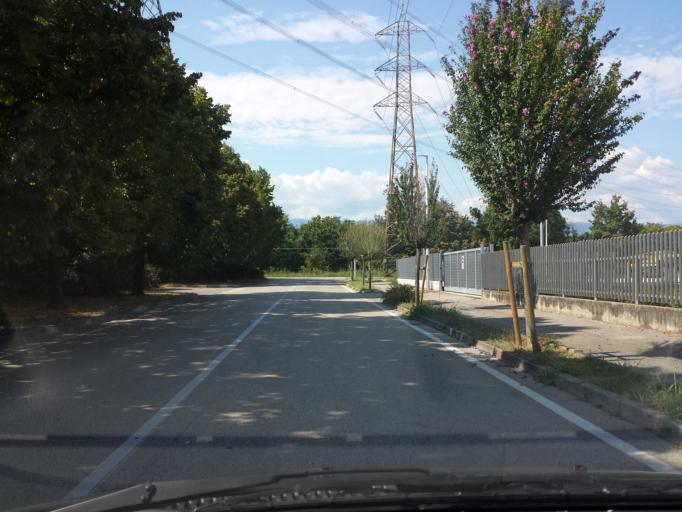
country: IT
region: Veneto
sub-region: Provincia di Vicenza
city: Montecchio Precalcino
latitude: 45.6691
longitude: 11.5721
